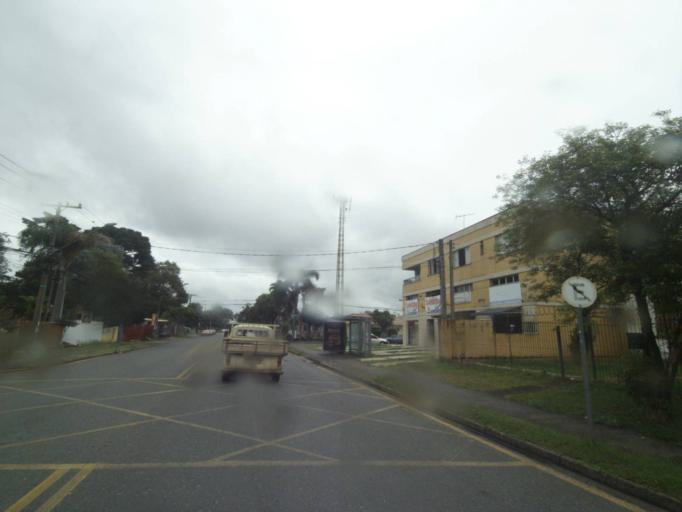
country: BR
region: Parana
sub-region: Curitiba
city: Curitiba
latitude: -25.4442
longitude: -49.3438
